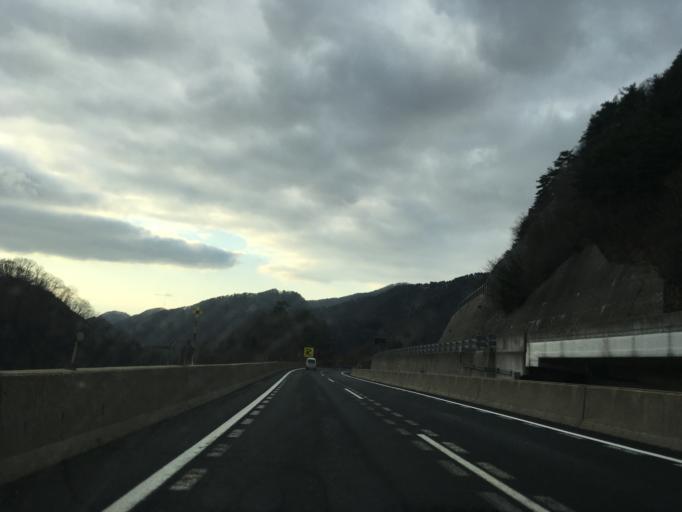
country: JP
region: Yamagata
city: Yamagata-shi
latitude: 38.2377
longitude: 140.4083
